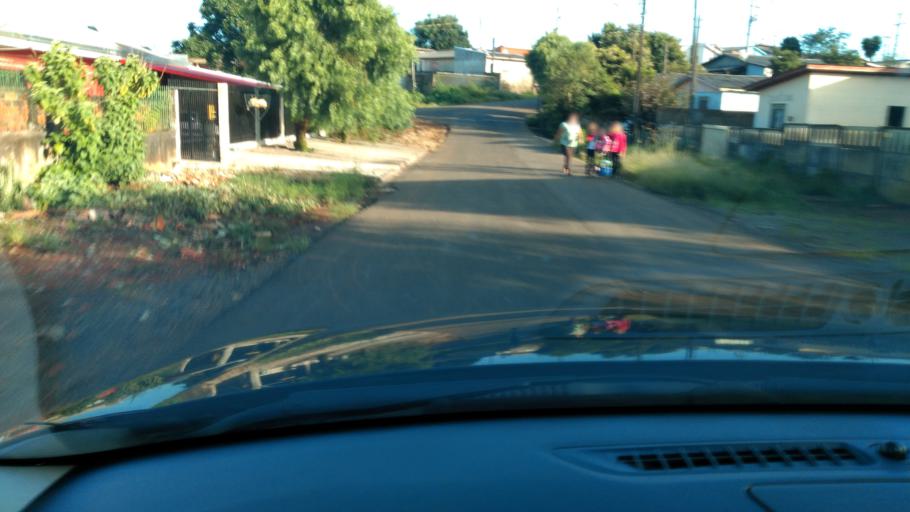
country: BR
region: Parana
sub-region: Guarapuava
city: Guarapuava
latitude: -25.3715
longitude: -51.4459
